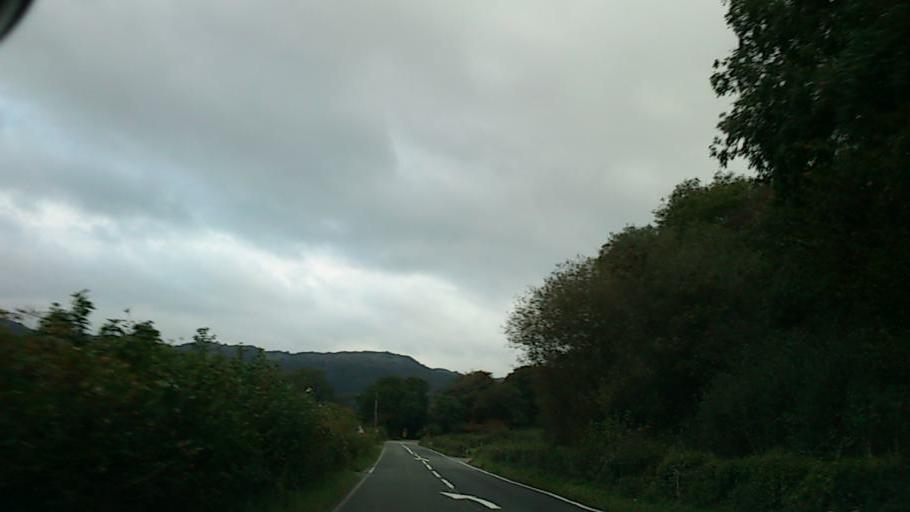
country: GB
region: Wales
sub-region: Sir Powys
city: Machynlleth
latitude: 52.5747
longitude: -3.9077
